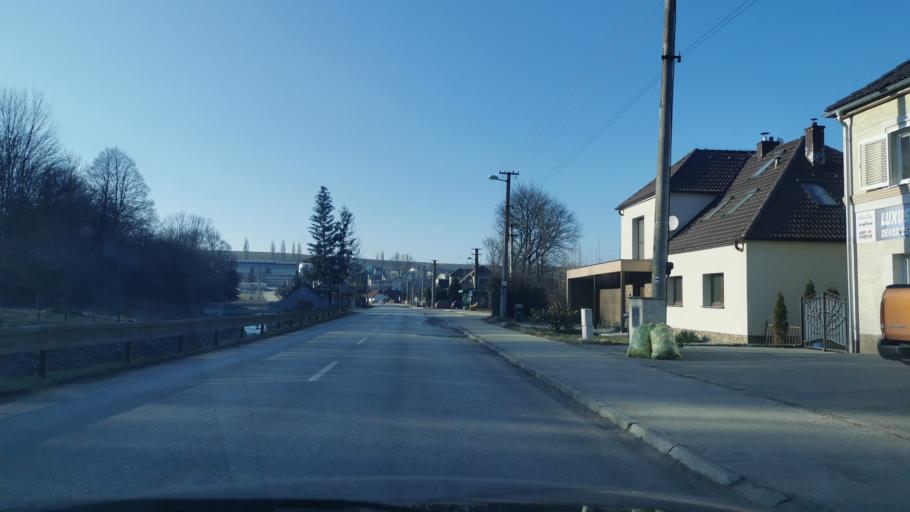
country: SK
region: Trenciansky
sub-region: Okres Myjava
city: Myjava
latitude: 48.7467
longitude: 17.5508
